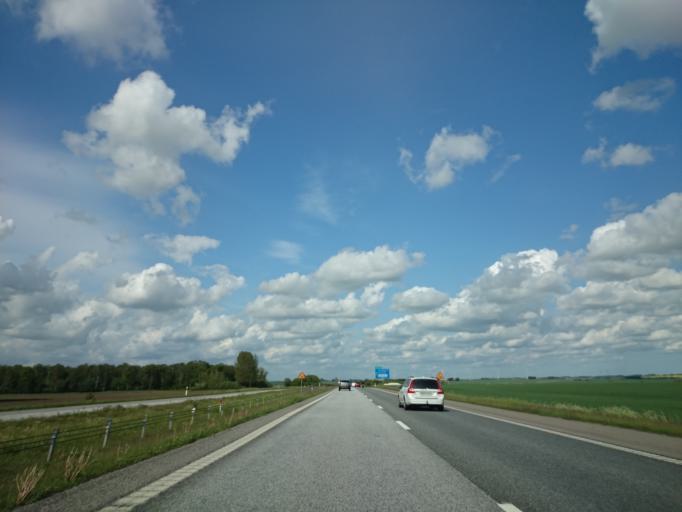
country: SE
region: Skane
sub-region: Eslovs Kommun
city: Eslov
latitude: 55.7622
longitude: 13.2941
